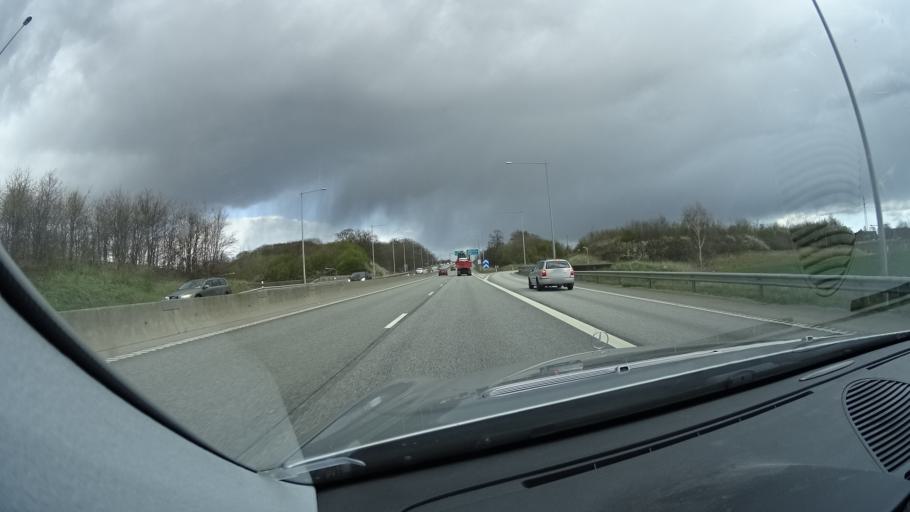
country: SE
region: Skane
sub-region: Burlovs Kommun
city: Arloev
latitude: 55.6354
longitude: 13.0933
